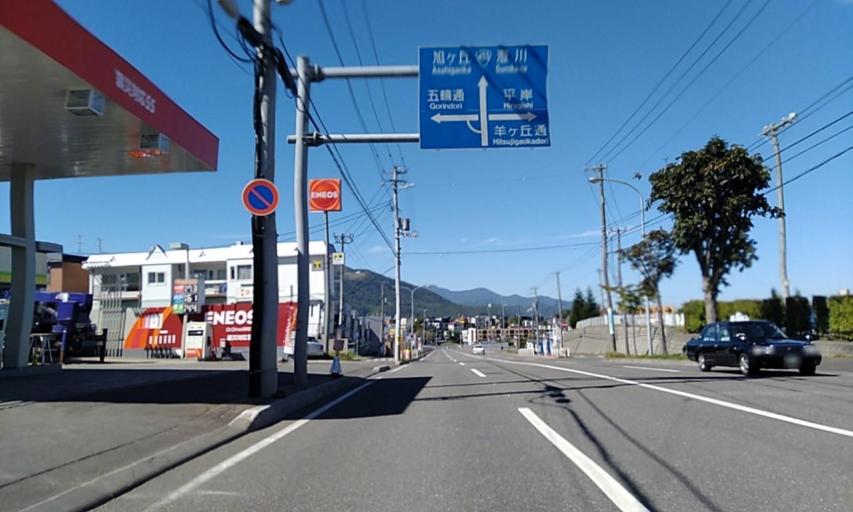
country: JP
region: Hokkaido
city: Sapporo
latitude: 43.0083
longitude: 141.3792
